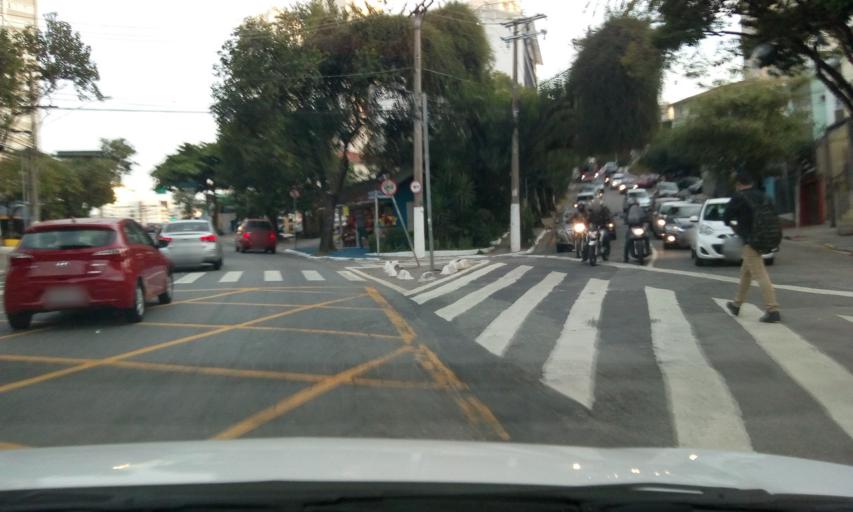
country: BR
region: Sao Paulo
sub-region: Sao Paulo
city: Sao Paulo
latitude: -23.5447
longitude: -46.6909
